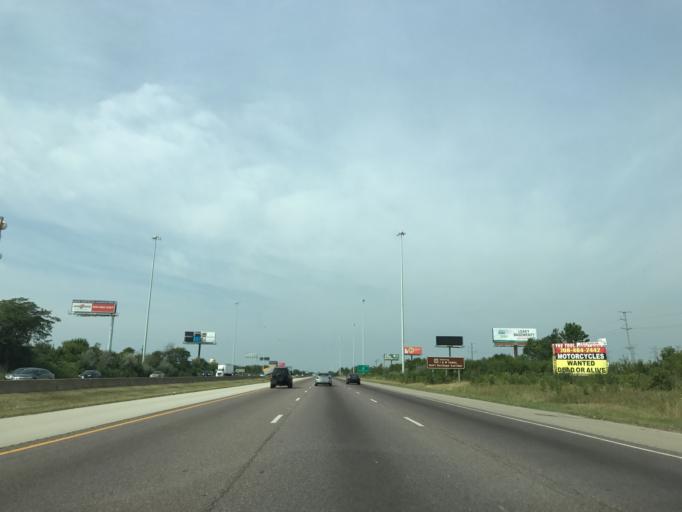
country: US
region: Illinois
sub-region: Cook County
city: Stickney
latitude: 41.8069
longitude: -87.7760
